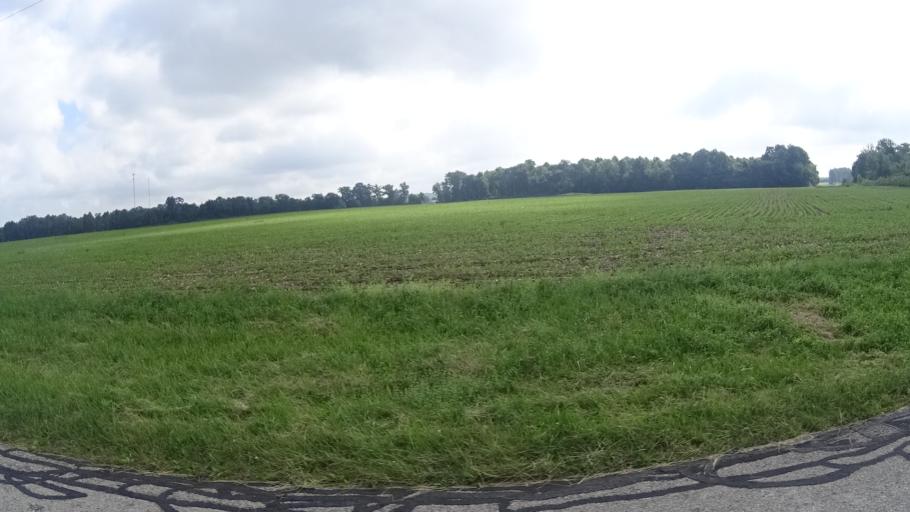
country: US
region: Ohio
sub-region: Huron County
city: Wakeman
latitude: 41.2969
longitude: -82.4554
